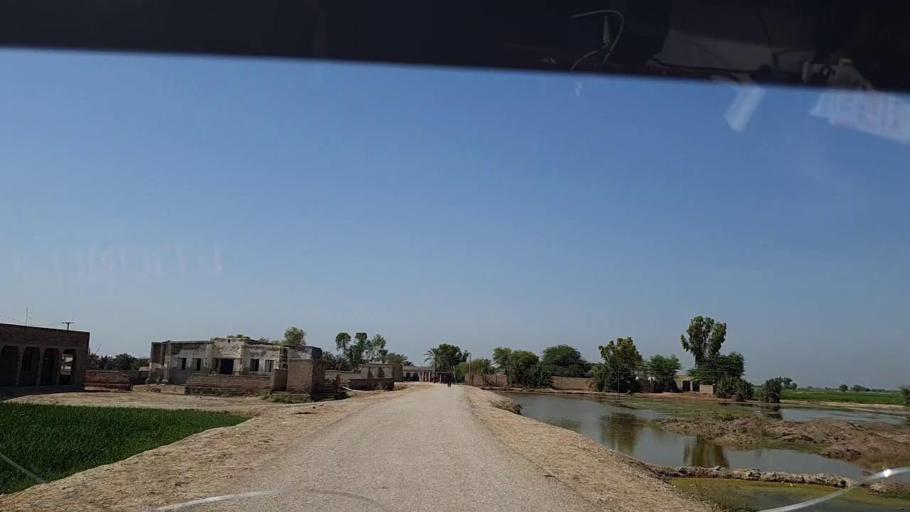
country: PK
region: Sindh
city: Tangwani
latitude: 28.3186
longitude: 69.0921
